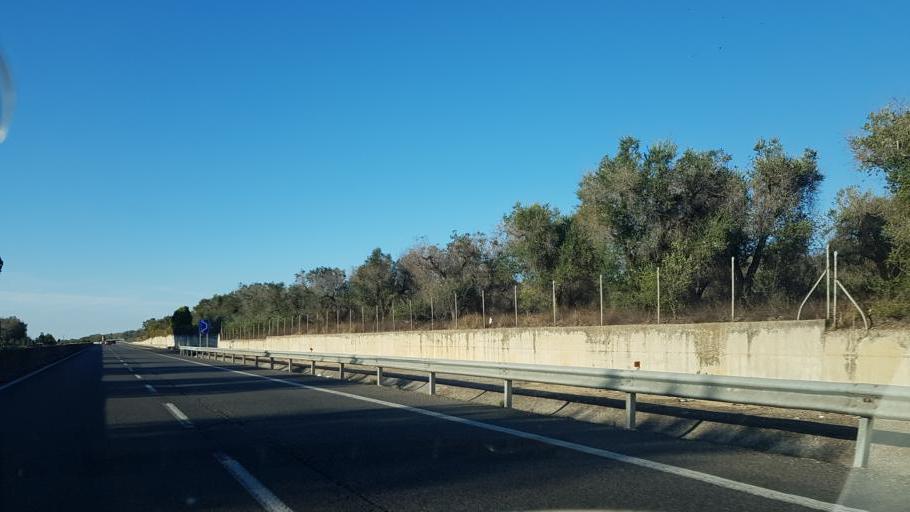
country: IT
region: Apulia
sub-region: Provincia di Brindisi
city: Torchiarolo
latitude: 40.4919
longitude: 18.0376
